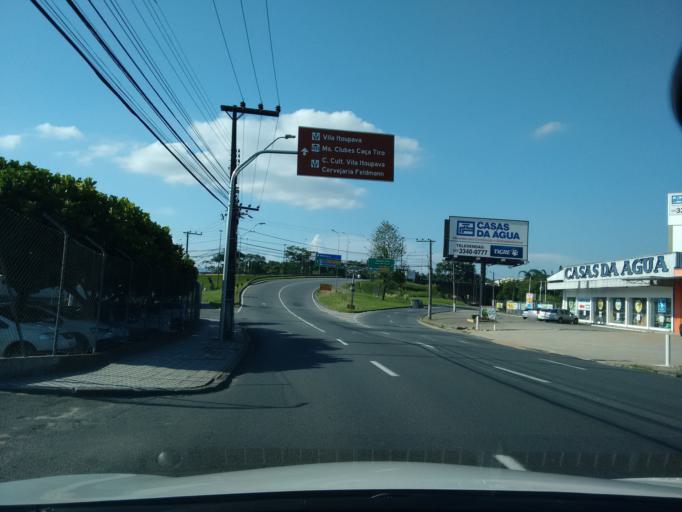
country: BR
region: Santa Catarina
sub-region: Blumenau
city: Blumenau
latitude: -26.9001
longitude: -49.0767
